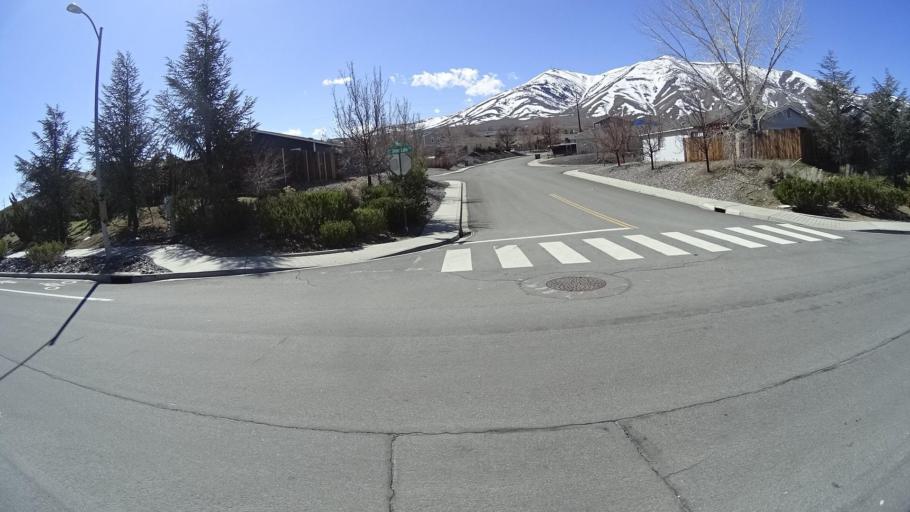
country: US
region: Nevada
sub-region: Washoe County
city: Lemmon Valley
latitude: 39.6265
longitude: -119.9041
